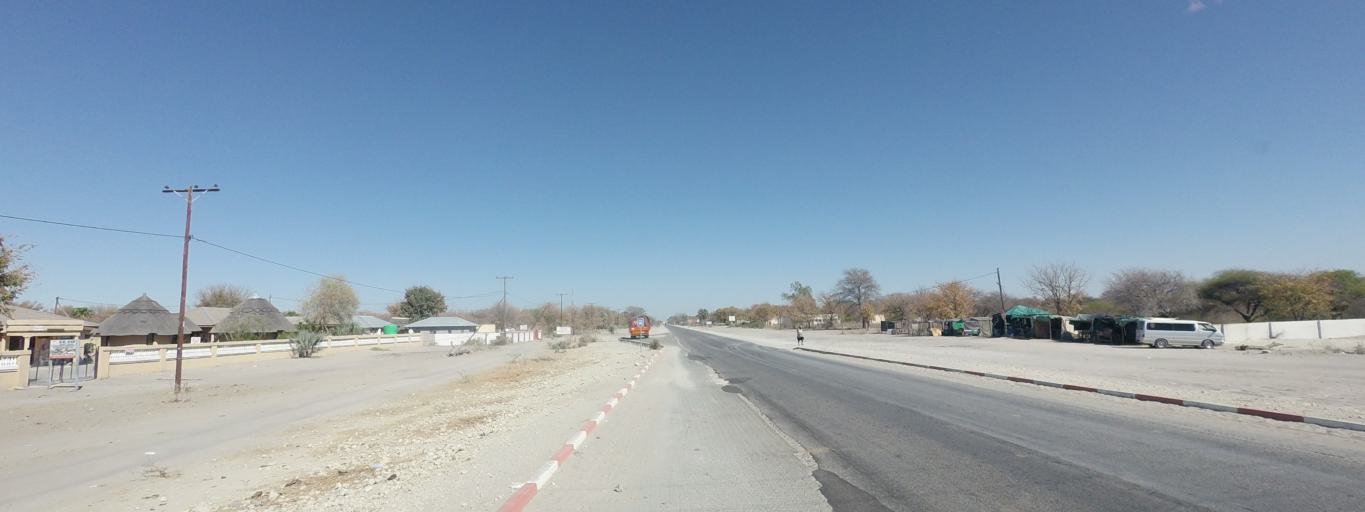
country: BW
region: Central
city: Nata
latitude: -20.2188
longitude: 26.1943
